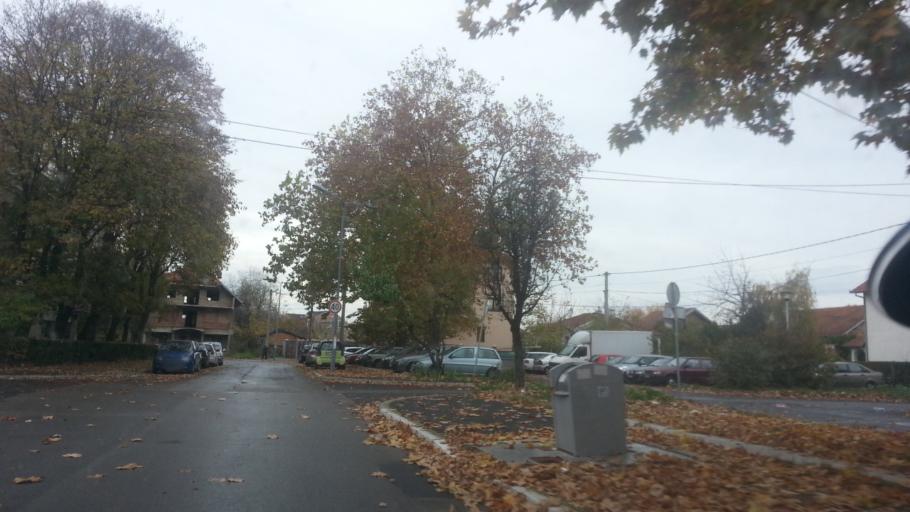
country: RS
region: Central Serbia
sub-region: Belgrade
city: Zemun
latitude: 44.8465
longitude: 20.3922
